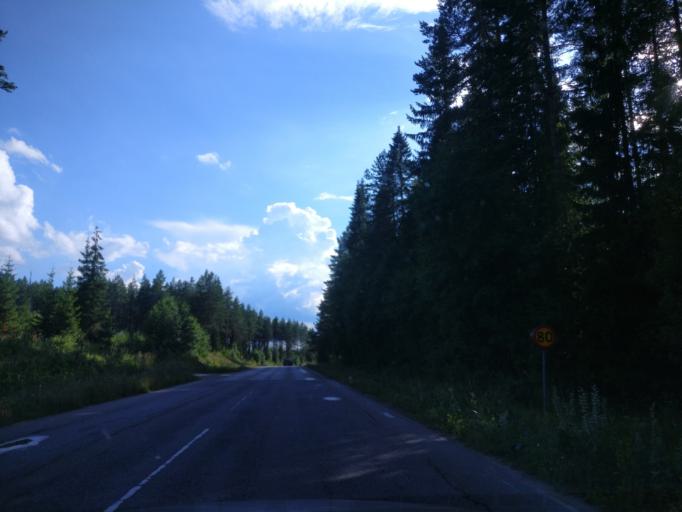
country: SE
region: Dalarna
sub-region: Ludvika Kommun
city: Ludvika
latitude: 60.2843
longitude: 15.0981
